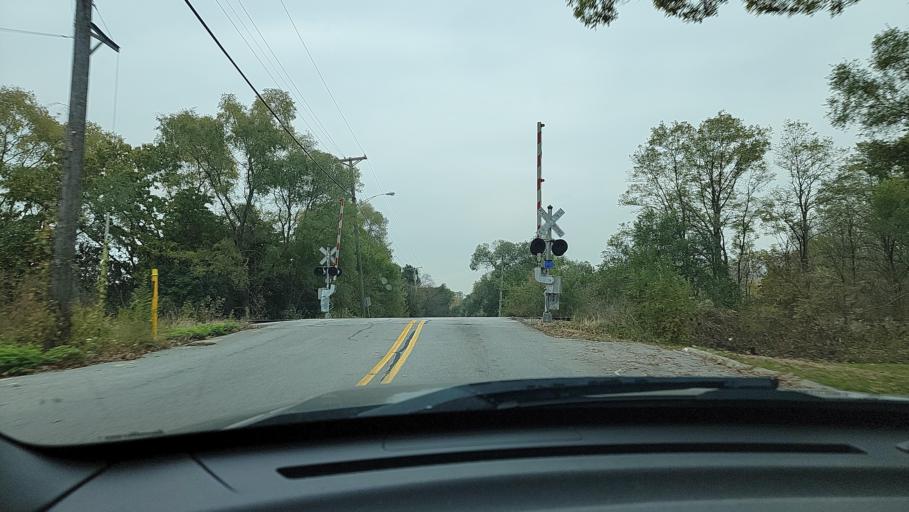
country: US
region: Indiana
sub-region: Lake County
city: Lake Station
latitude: 41.5822
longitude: -87.2123
